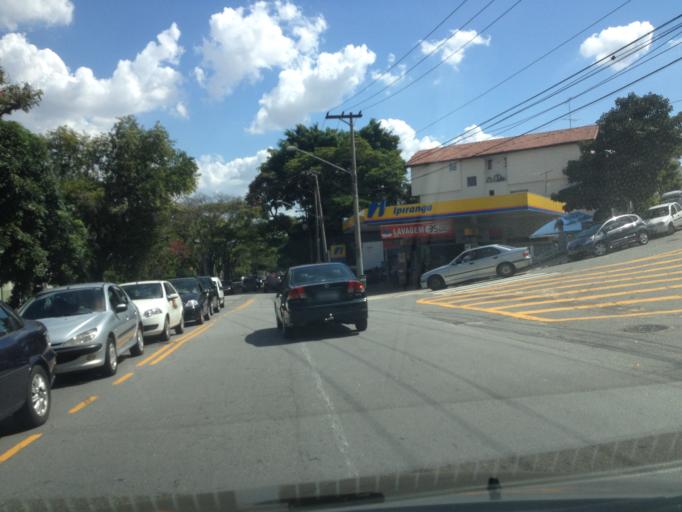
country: BR
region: Sao Paulo
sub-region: Sao Paulo
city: Sao Paulo
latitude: -23.5458
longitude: -46.7029
